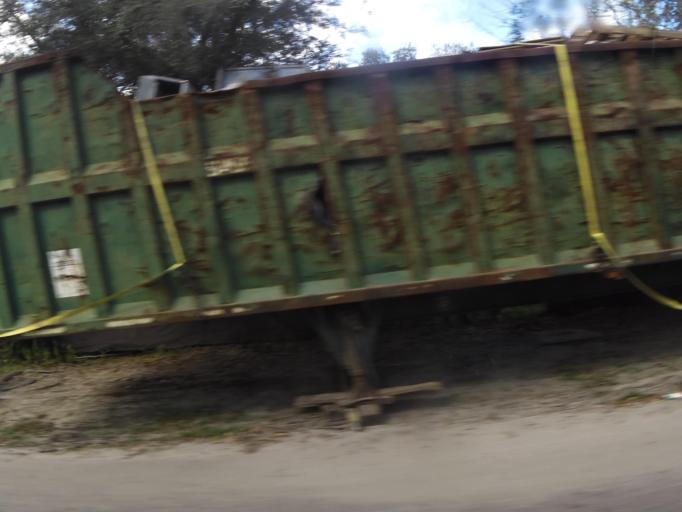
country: US
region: Florida
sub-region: Duval County
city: Jacksonville
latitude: 30.3412
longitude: -81.7029
